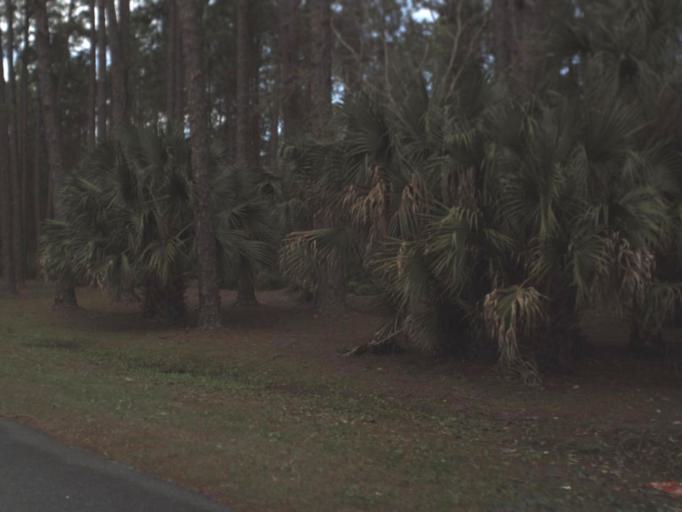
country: US
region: Florida
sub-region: Franklin County
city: Apalachicola
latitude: 29.7162
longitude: -85.0401
